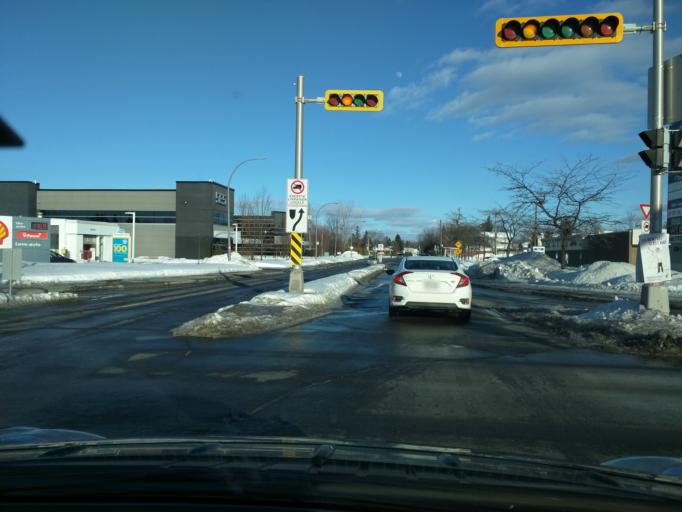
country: CA
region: Quebec
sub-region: Laurentides
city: Rosemere
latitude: 45.5917
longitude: -73.7867
